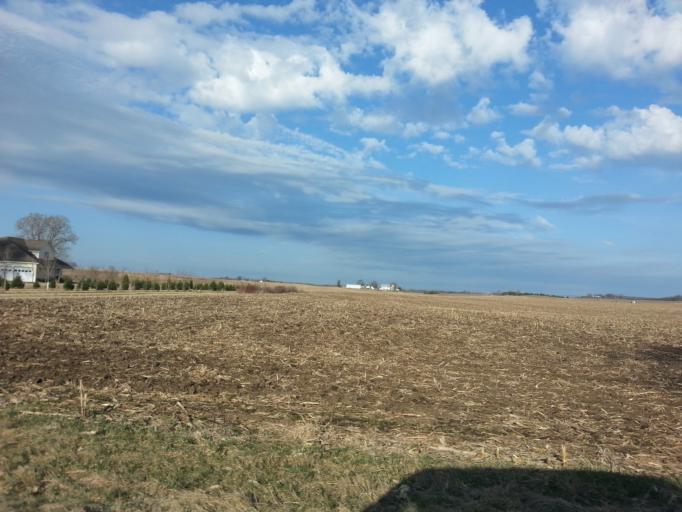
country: US
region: Minnesota
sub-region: Washington County
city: Afton
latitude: 44.8391
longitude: -92.8420
